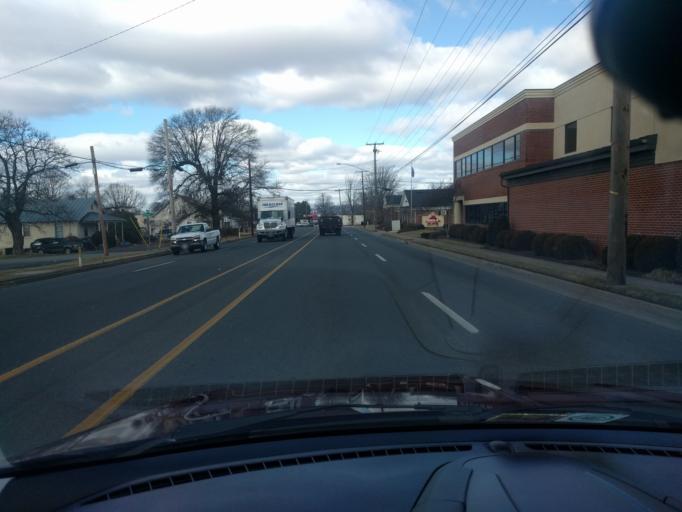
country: US
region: Virginia
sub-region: City of Lynchburg
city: Lynchburg
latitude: 37.3814
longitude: -79.1363
